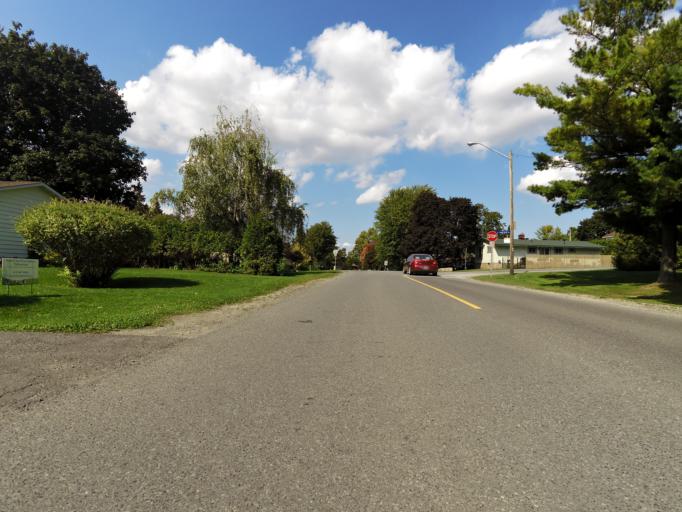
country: CA
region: Ontario
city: Bells Corners
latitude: 45.2388
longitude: -75.6986
